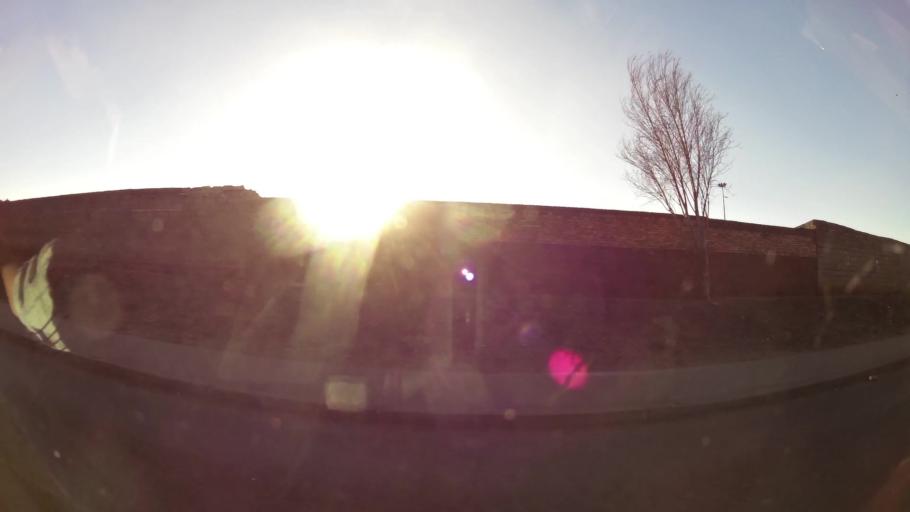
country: ZA
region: Gauteng
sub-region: Ekurhuleni Metropolitan Municipality
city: Tembisa
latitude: -26.0146
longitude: 28.2408
